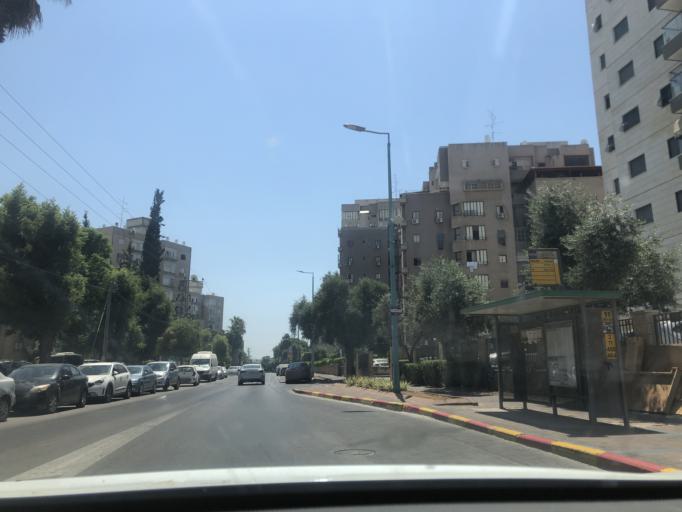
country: IL
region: Central District
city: Lod
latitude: 31.9447
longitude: 34.8937
